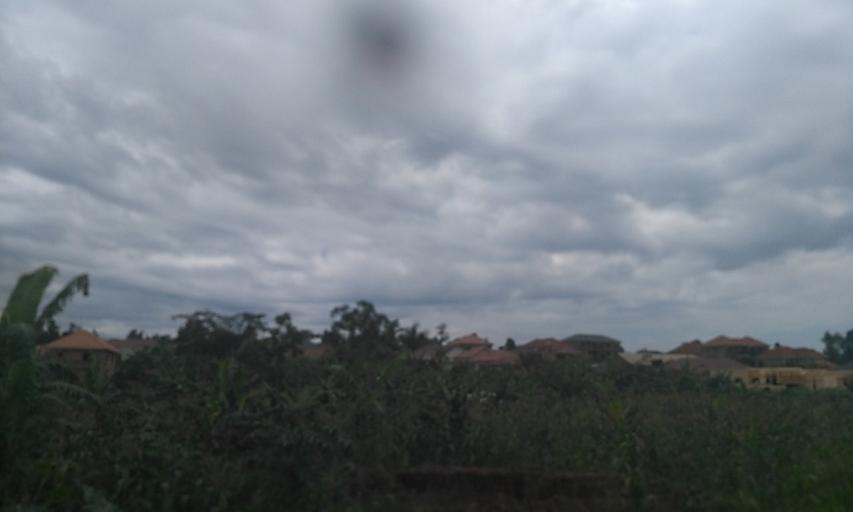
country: UG
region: Central Region
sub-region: Wakiso District
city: Bweyogerere
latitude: 0.3969
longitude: 32.6771
